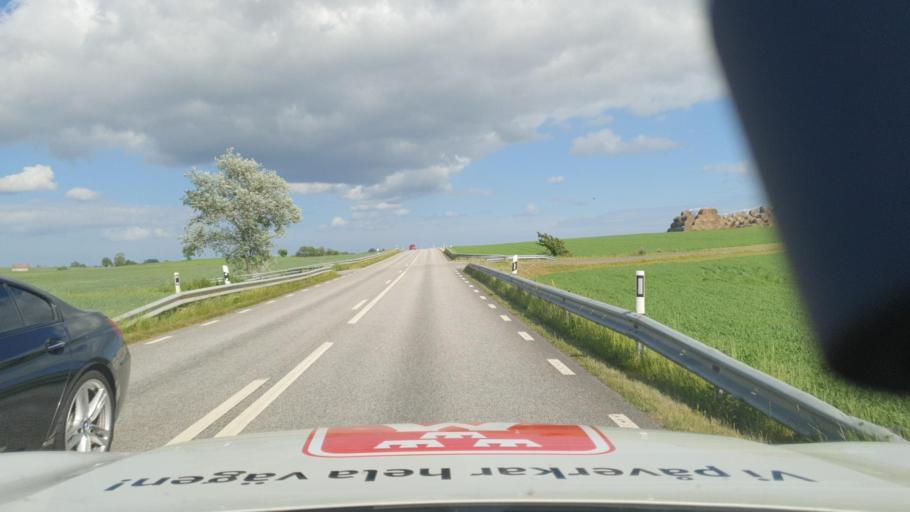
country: SE
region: Skane
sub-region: Simrishamns Kommun
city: Kivik
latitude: 55.5569
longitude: 14.1317
